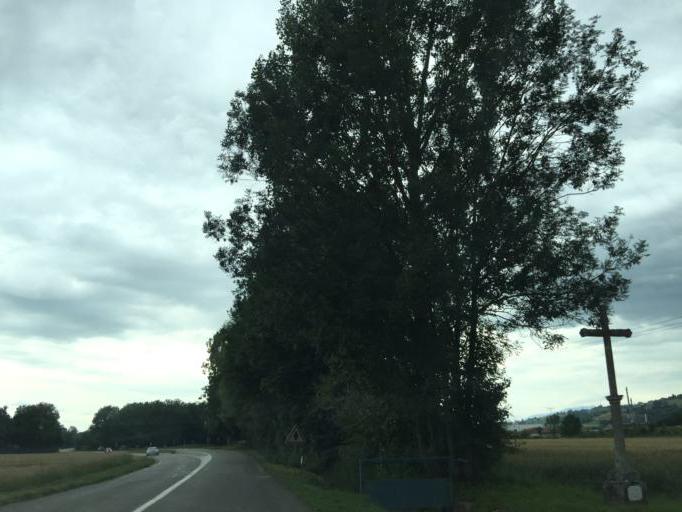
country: FR
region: Rhone-Alpes
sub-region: Departement de l'Isere
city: Romagnieu
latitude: 45.5695
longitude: 5.6605
